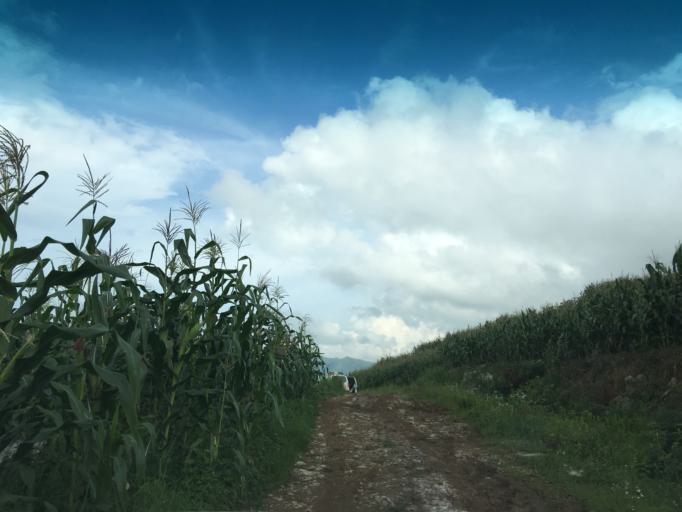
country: CN
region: Guangxi Zhuangzu Zizhiqu
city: Xinzhou
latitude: 24.9920
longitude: 105.6350
